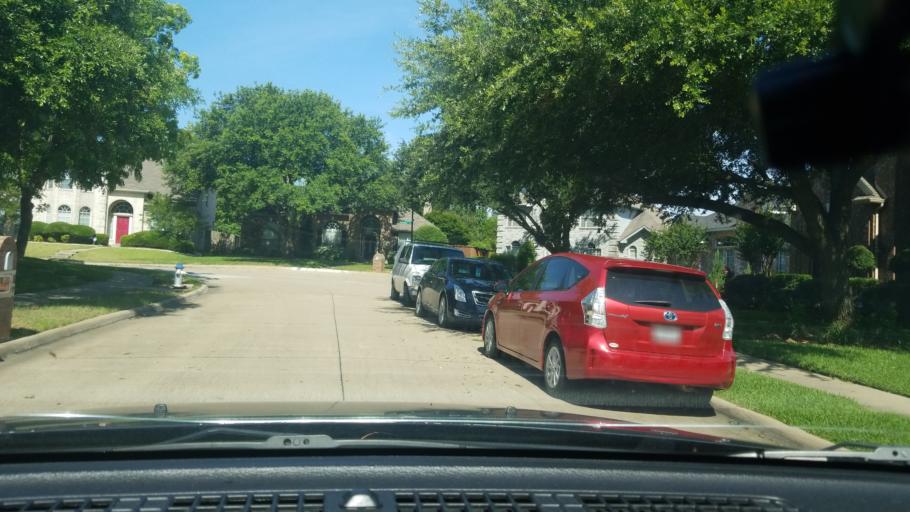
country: US
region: Texas
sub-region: Dallas County
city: Mesquite
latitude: 32.7794
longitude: -96.5846
